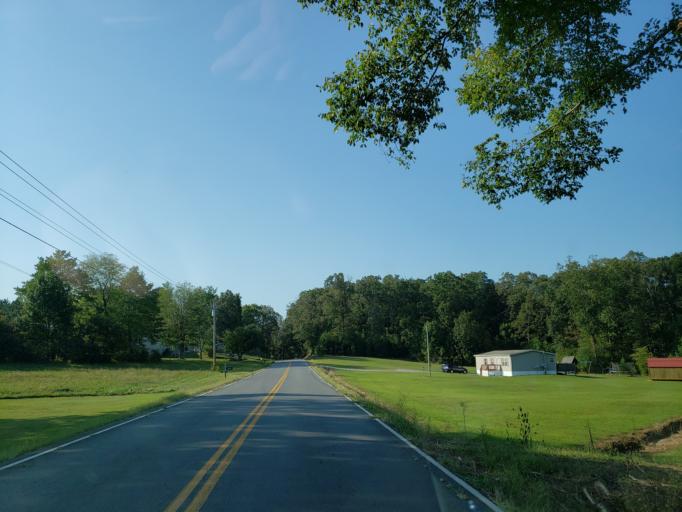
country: US
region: Tennessee
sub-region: Bradley County
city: Wildwood Lake
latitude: 35.0404
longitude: -84.7437
